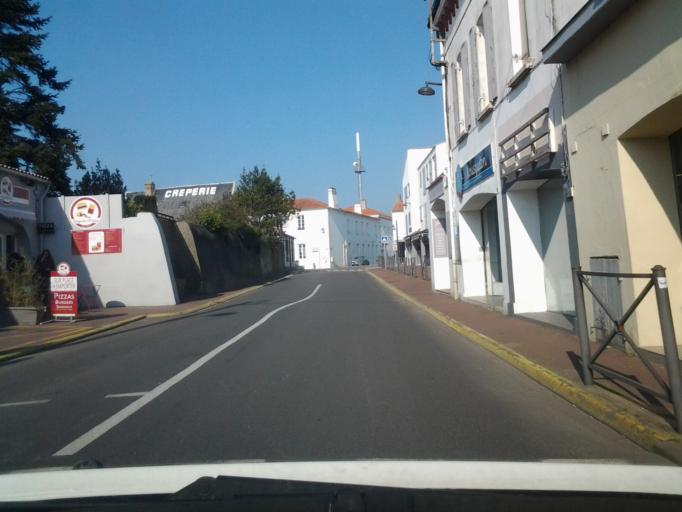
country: FR
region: Pays de la Loire
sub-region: Departement de la Vendee
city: La Gueriniere
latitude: 47.0006
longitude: -2.2475
